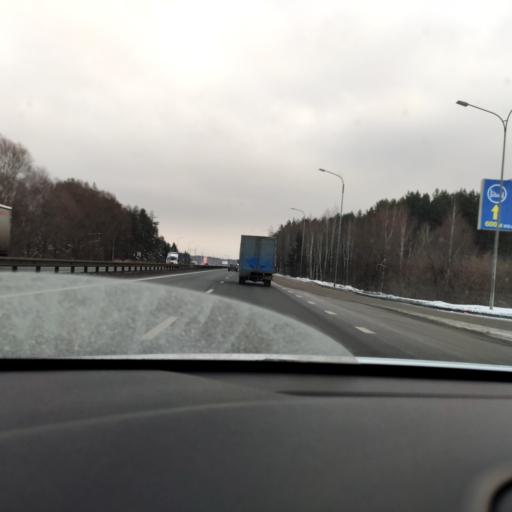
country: RU
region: Tatarstan
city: Vysokaya Gora
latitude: 55.9044
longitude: 49.1837
